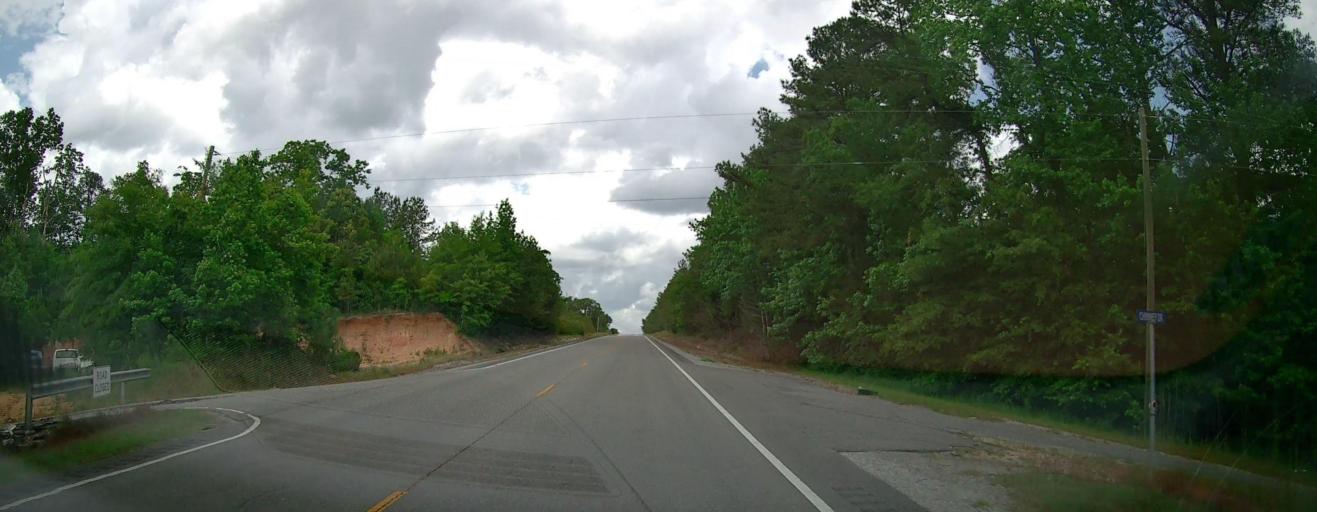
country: US
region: Alabama
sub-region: Marion County
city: Hamilton
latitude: 34.1306
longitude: -88.0266
